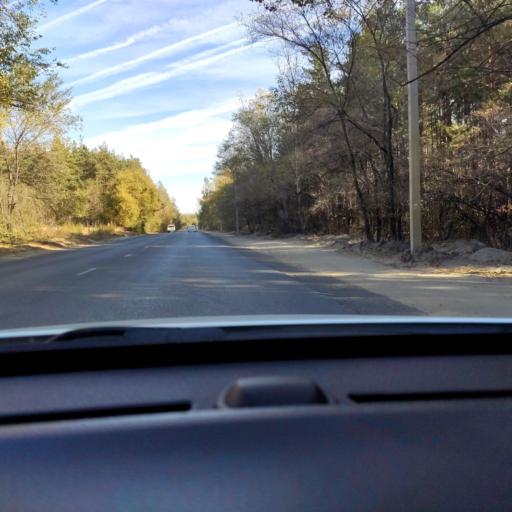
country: RU
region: Voronezj
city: Pridonskoy
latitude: 51.6851
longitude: 39.0991
